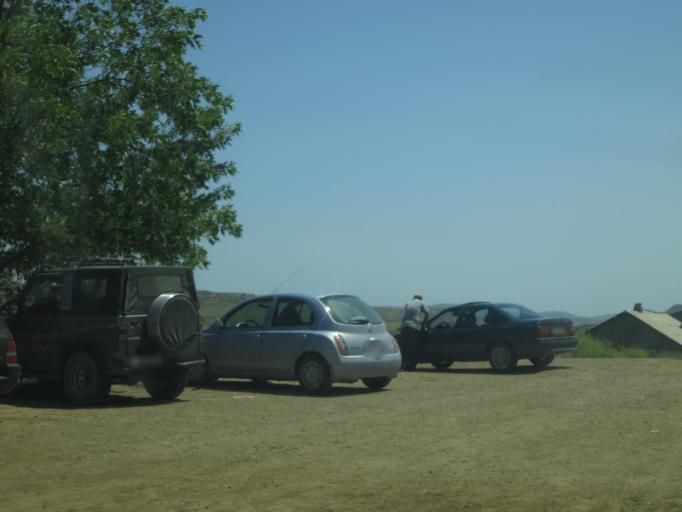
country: AZ
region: Agstafa
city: Saloglu
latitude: 41.4494
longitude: 45.3756
